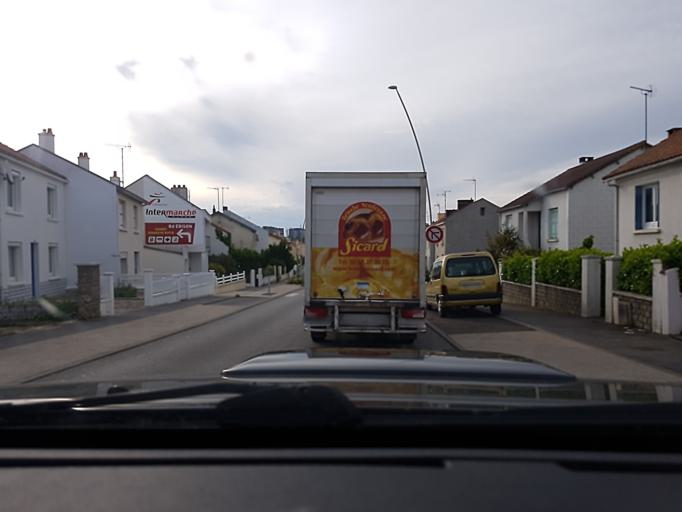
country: FR
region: Pays de la Loire
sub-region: Departement de la Vendee
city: La Roche-sur-Yon
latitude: 46.6821
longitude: -1.4431
